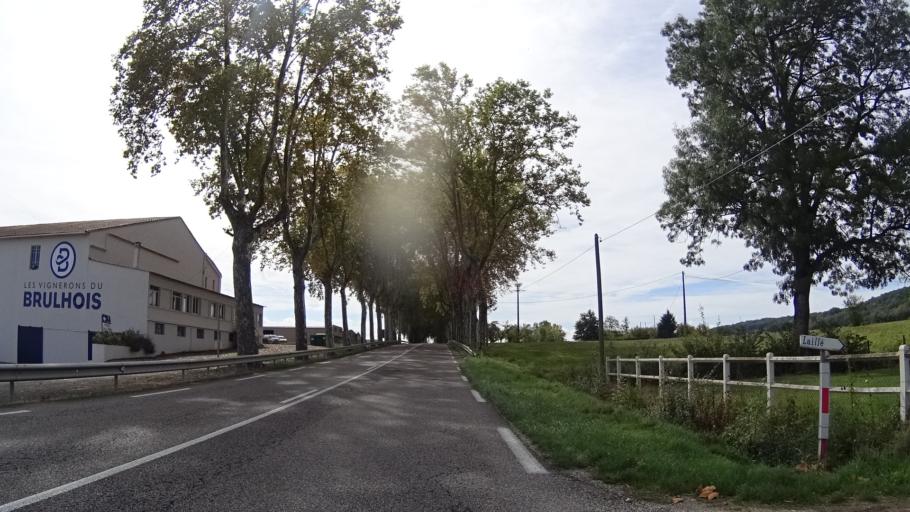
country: FR
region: Aquitaine
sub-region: Departement du Lot-et-Garonne
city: Layrac
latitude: 44.1121
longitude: 0.6568
